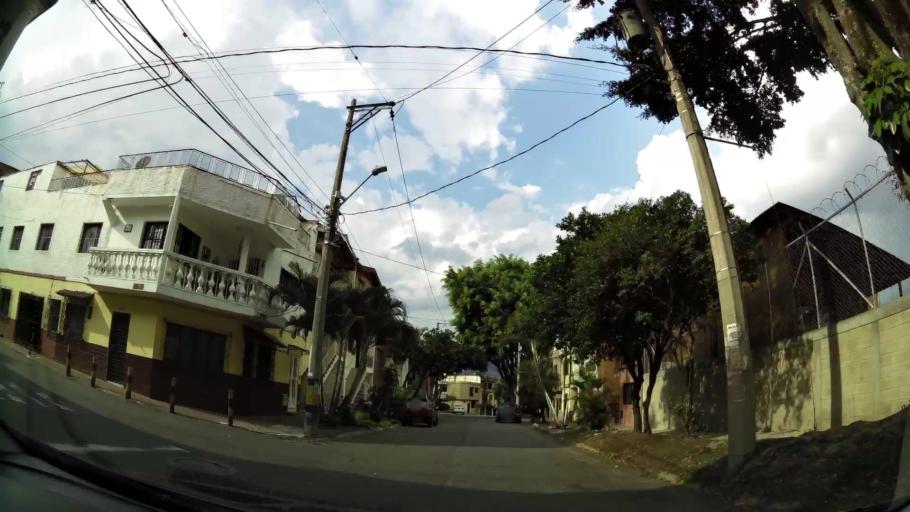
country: CO
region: Antioquia
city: Medellin
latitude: 6.2512
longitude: -75.5957
